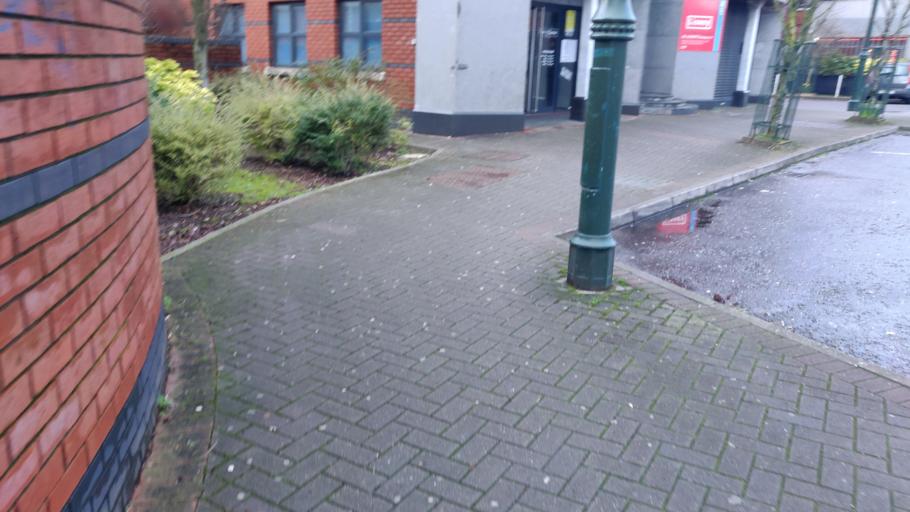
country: IE
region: Munster
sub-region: County Cork
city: Cork
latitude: 51.8771
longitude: -8.4352
